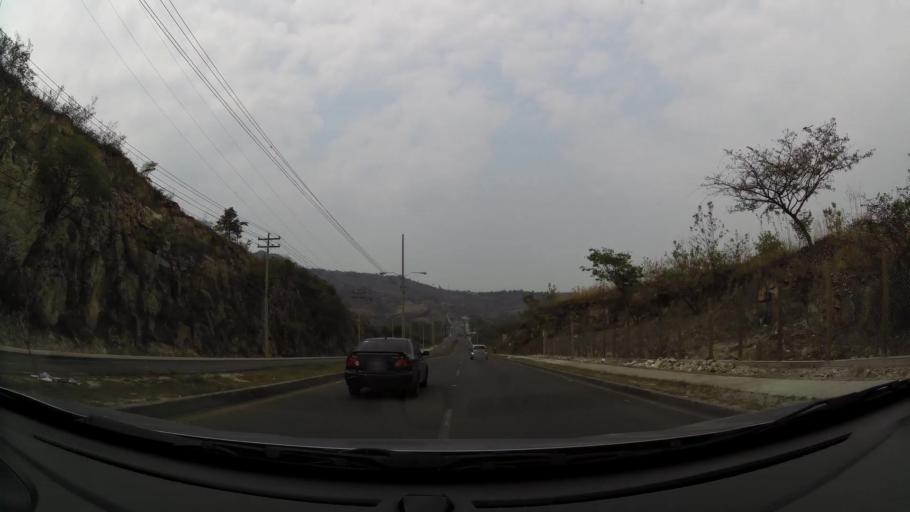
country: HN
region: Francisco Morazan
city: Tegucigalpa
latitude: 14.0628
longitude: -87.2537
